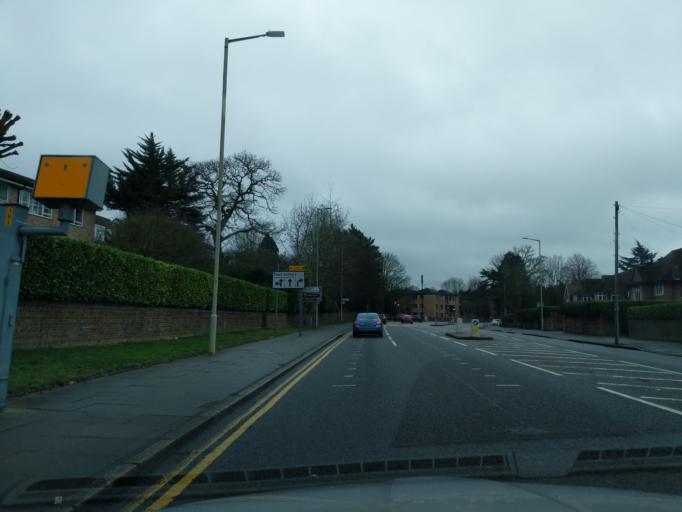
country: GB
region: England
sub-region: Hertfordshire
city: Watford
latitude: 51.6703
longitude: -0.4146
